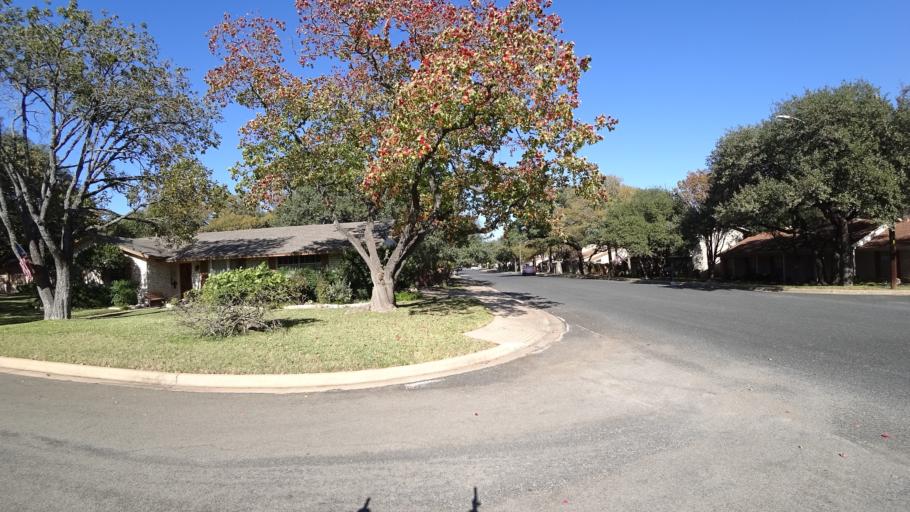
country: US
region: Texas
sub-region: Williamson County
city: Jollyville
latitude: 30.3713
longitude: -97.7505
